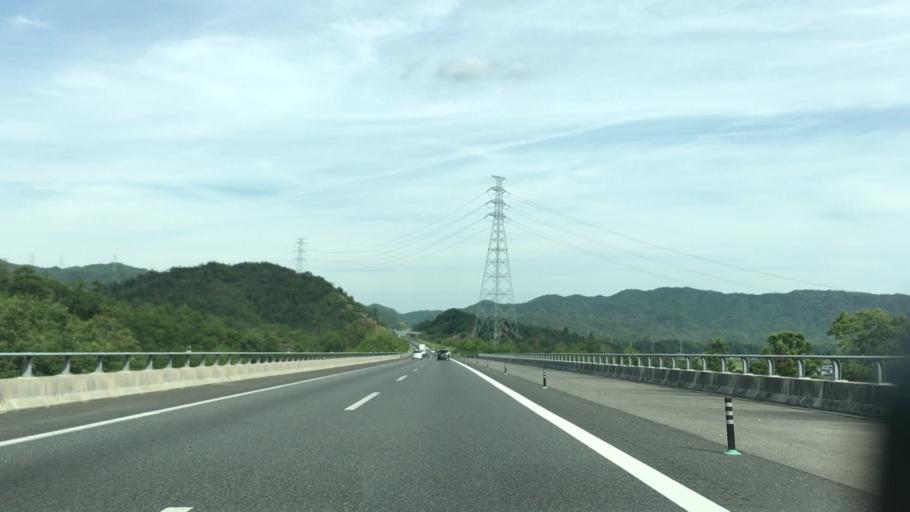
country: JP
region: Shiga Prefecture
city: Minakuchicho-matoba
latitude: 34.9298
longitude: 136.0593
